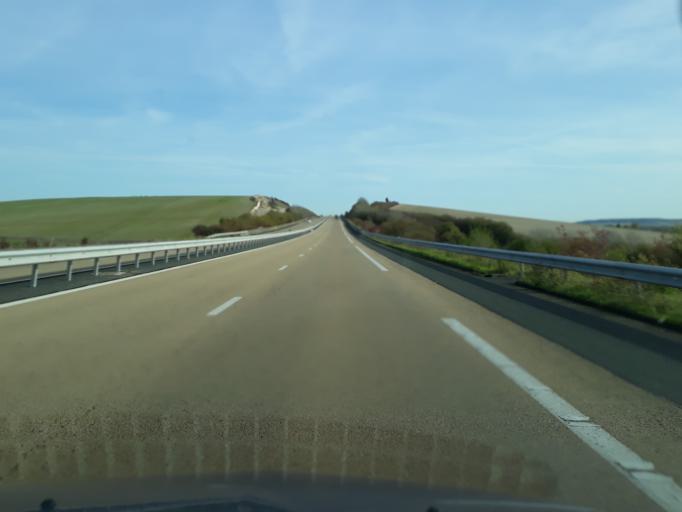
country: FR
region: Champagne-Ardenne
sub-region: Departement de l'Aube
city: Estissac
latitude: 48.2723
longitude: 3.7751
